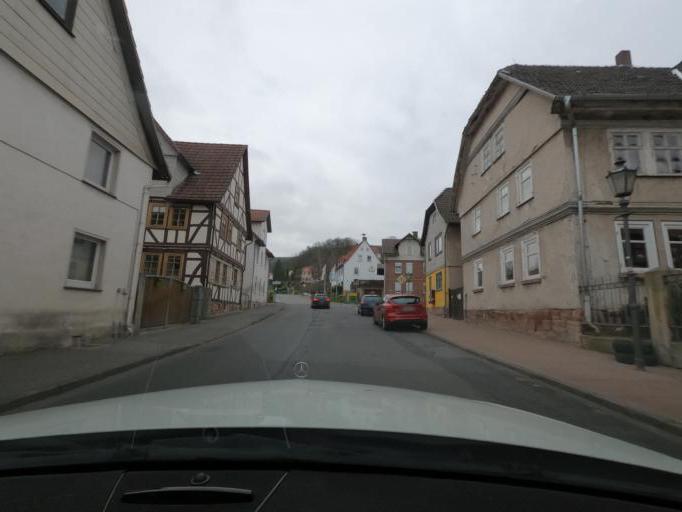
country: DE
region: Hesse
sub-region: Regierungsbezirk Kassel
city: Eschwege
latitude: 51.2057
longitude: 10.0646
